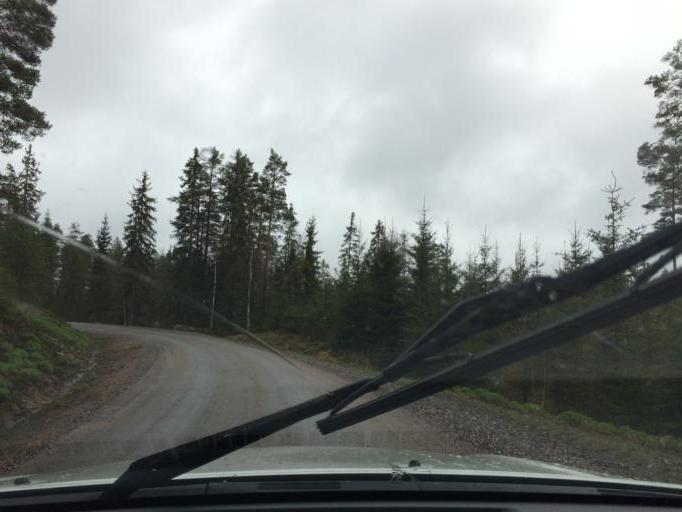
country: SE
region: OErebro
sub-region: Hallefors Kommun
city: Haellefors
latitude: 60.0268
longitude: 14.5566
